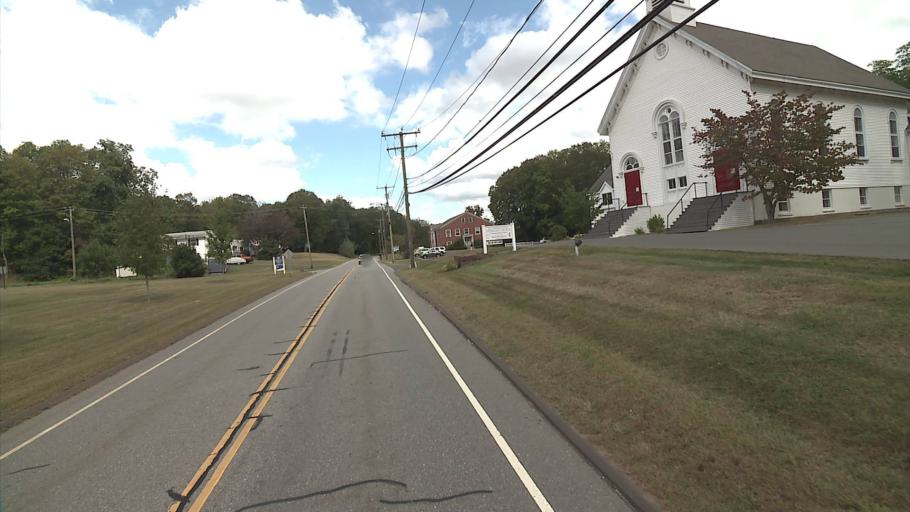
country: US
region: Connecticut
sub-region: Middlesex County
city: Durham
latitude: 41.5177
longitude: -72.7105
